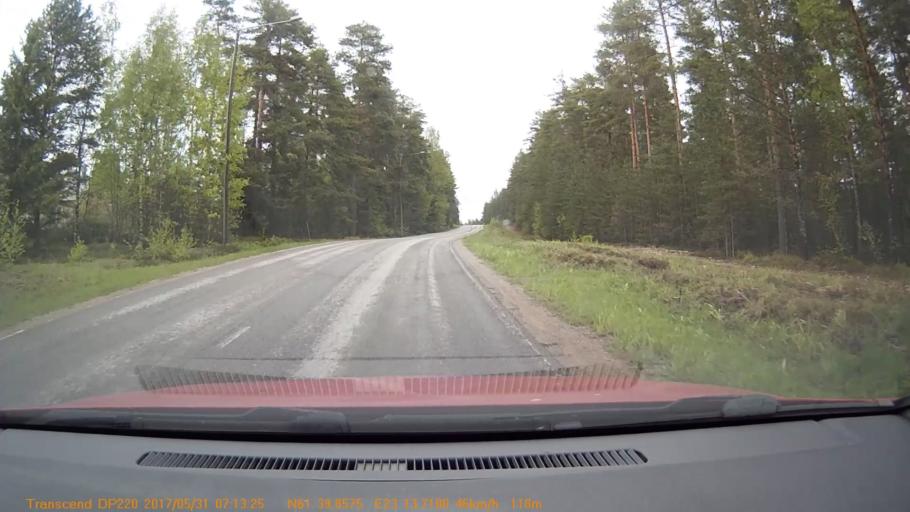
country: FI
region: Pirkanmaa
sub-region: Tampere
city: Haemeenkyroe
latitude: 61.6643
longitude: 23.2285
